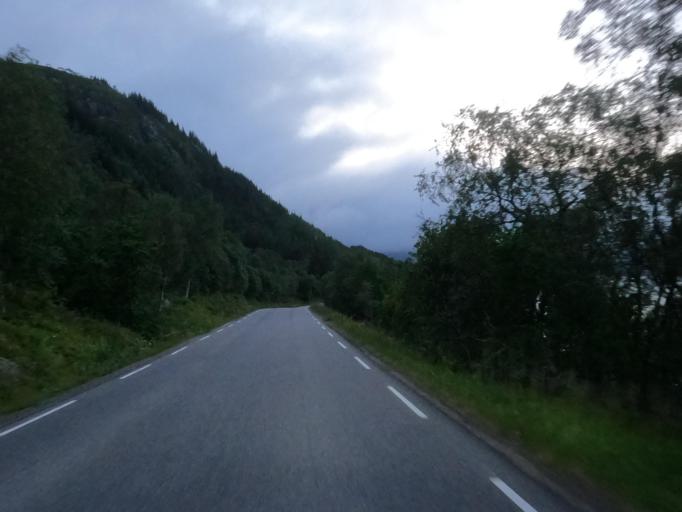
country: NO
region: Nordland
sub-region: Lodingen
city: Lodingen
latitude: 68.5934
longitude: 15.7890
